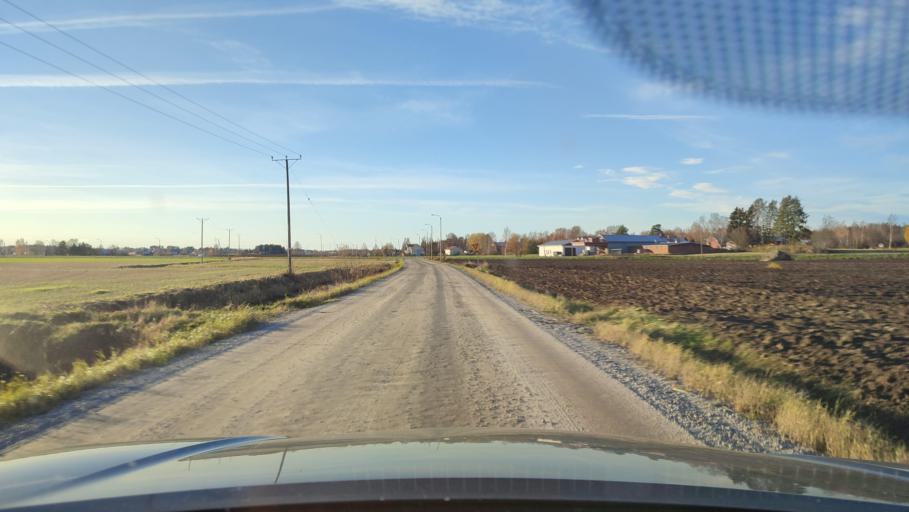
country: FI
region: Ostrobothnia
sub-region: Vaasa
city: Ristinummi
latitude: 63.0106
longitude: 21.7040
